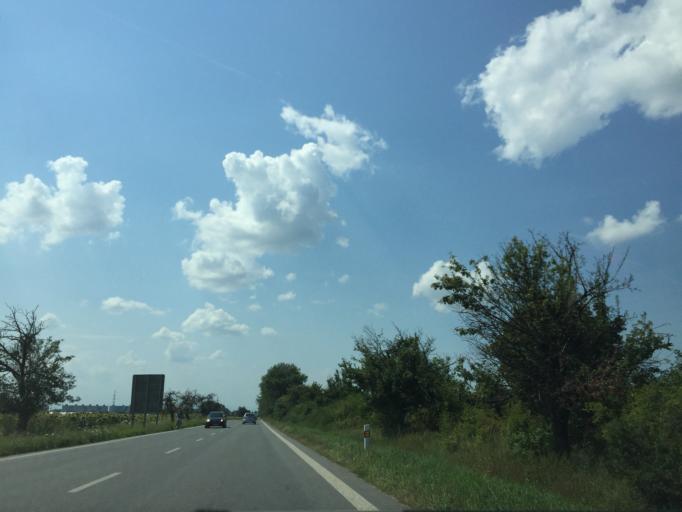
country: SK
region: Kosicky
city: Sobrance
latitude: 48.7396
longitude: 22.2018
